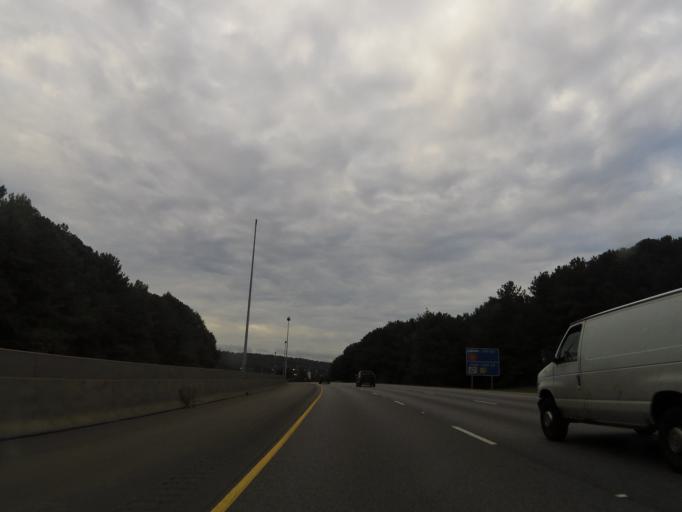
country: US
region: Alabama
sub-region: Jefferson County
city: Cahaba Heights
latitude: 33.4754
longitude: -86.7057
